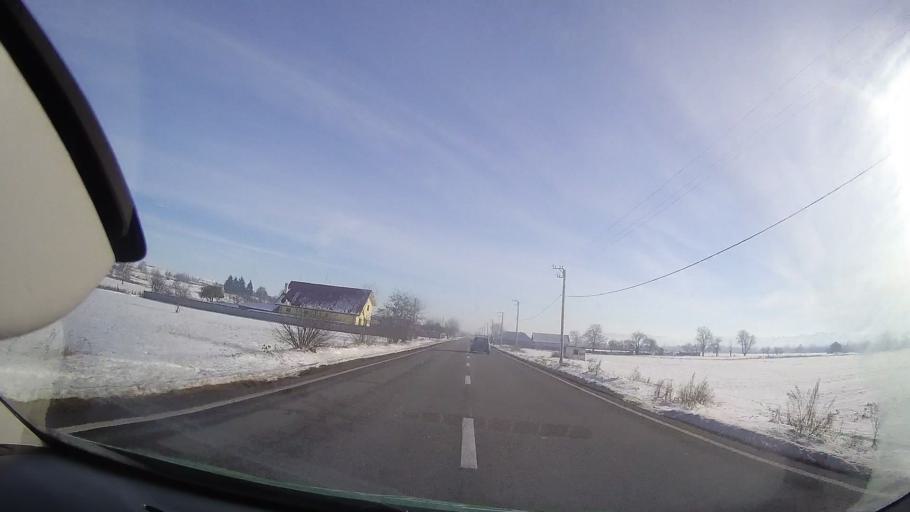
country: RO
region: Neamt
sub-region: Comuna Ghindaoani
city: Ghindaoani
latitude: 47.0811
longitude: 26.3438
